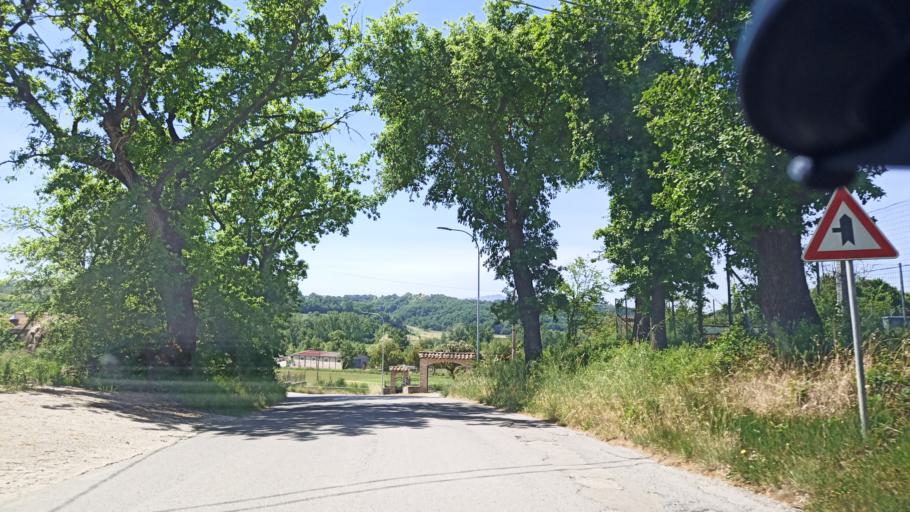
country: IT
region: Latium
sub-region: Provincia di Rieti
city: Forano
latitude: 42.3207
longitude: 12.5869
